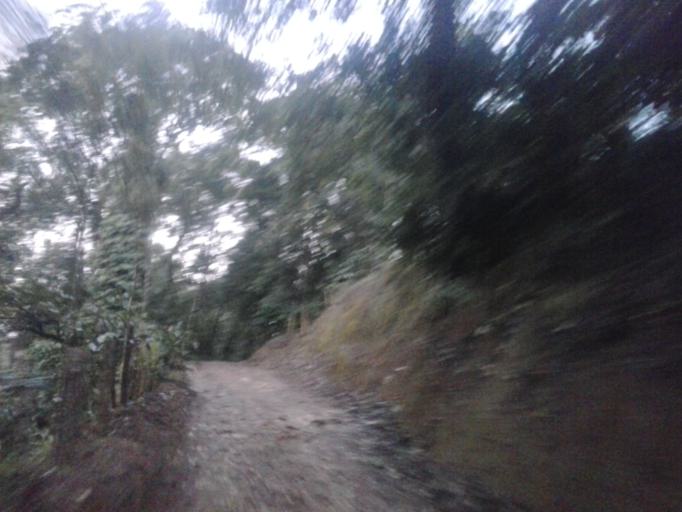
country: IN
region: Karnataka
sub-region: Chikmagalur
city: Mudigere
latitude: 13.0137
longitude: 75.6692
